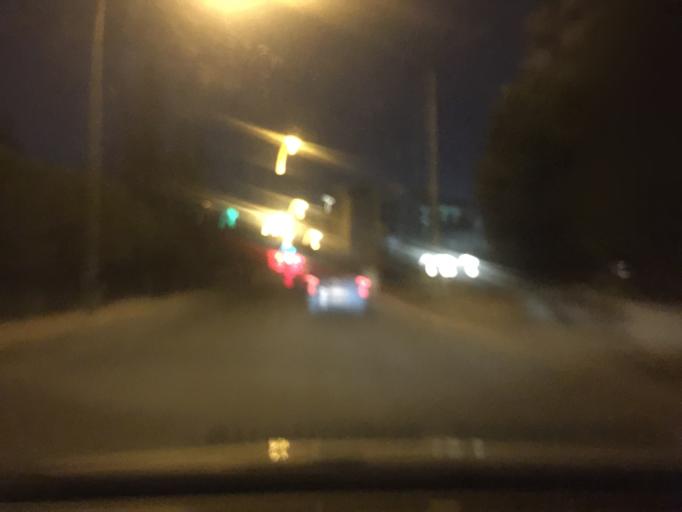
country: JO
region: Amman
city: Amman
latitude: 31.9812
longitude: 35.9175
